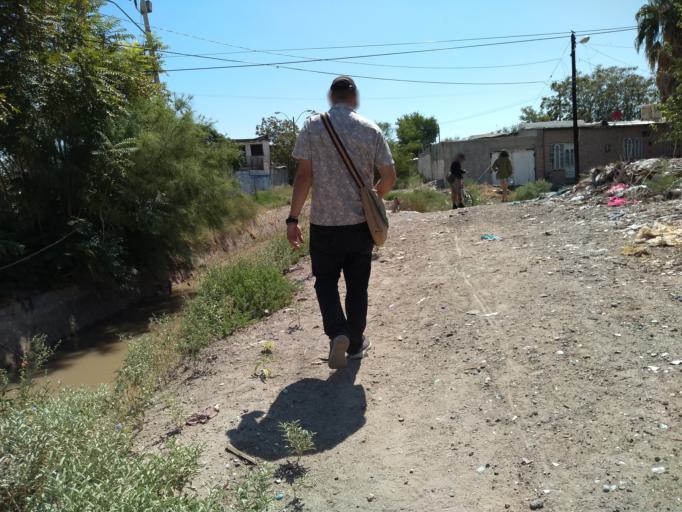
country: US
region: Texas
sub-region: El Paso County
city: El Paso
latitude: 31.7476
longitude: -106.4935
